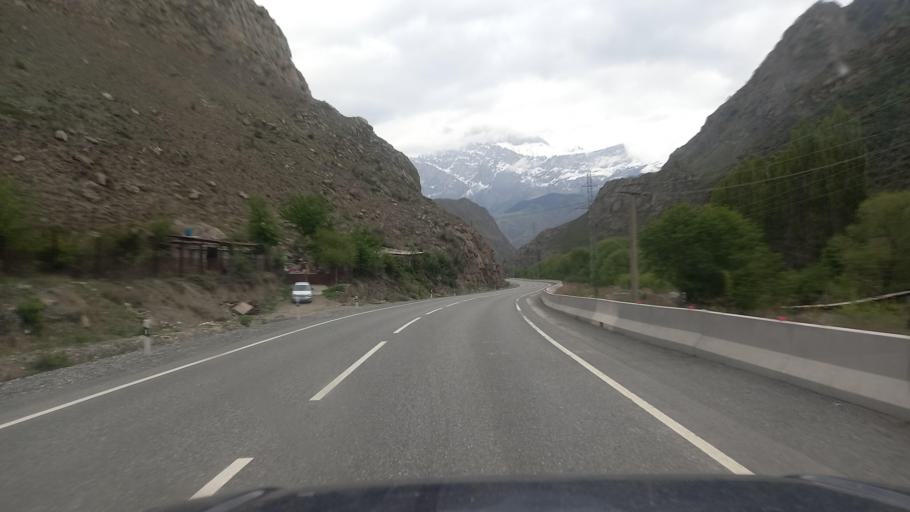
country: RU
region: North Ossetia
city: Mizur
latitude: 42.8554
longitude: 44.0953
